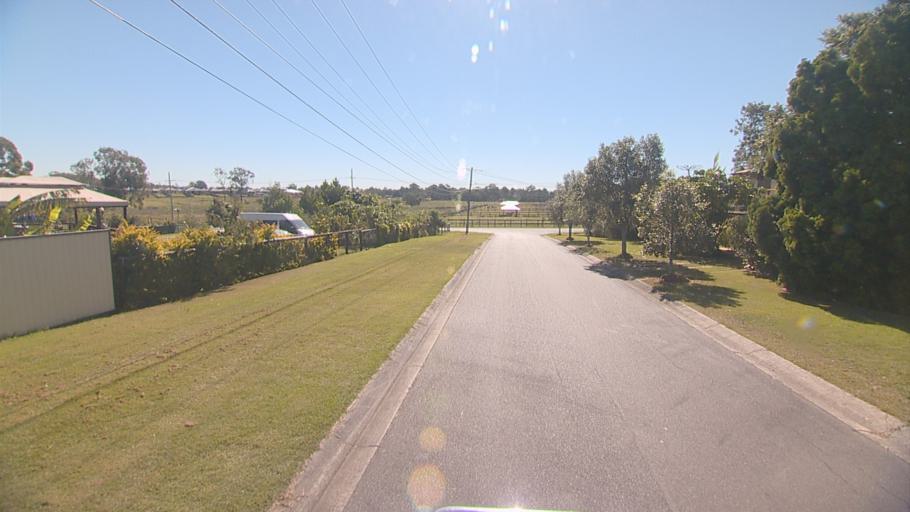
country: AU
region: Queensland
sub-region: Logan
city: Waterford West
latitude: -27.6889
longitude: 153.1420
